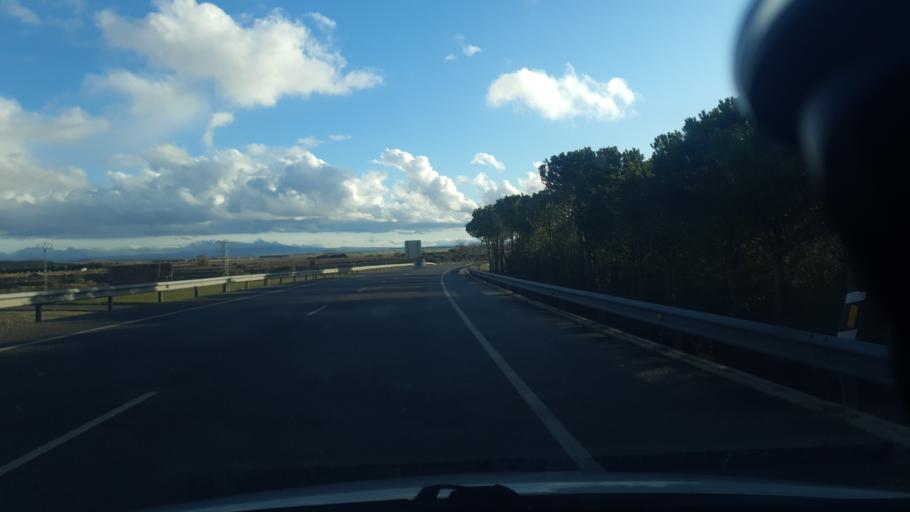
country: ES
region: Castille and Leon
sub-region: Provincia de Segovia
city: Codorniz
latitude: 41.0466
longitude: -4.6223
